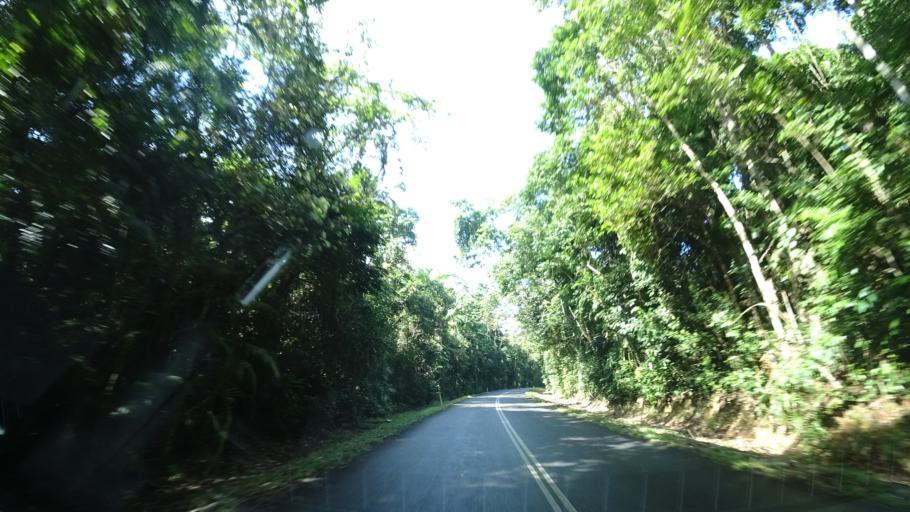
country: AU
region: Queensland
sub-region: Cairns
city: Port Douglas
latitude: -16.1455
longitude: 145.4394
